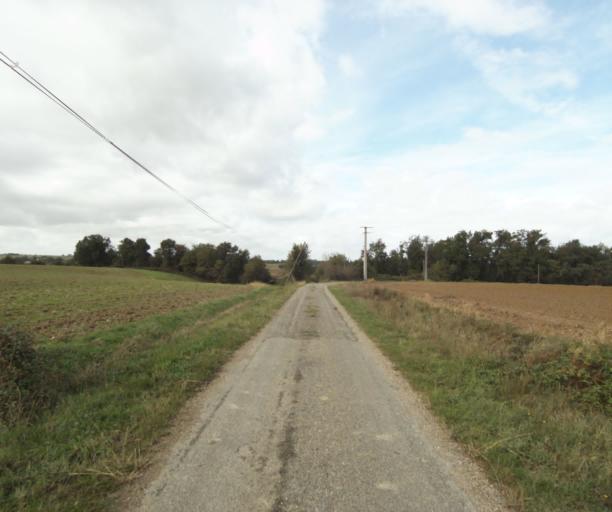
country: FR
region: Midi-Pyrenees
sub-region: Departement du Tarn-et-Garonne
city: Beaumont-de-Lomagne
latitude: 43.8783
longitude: 1.0729
